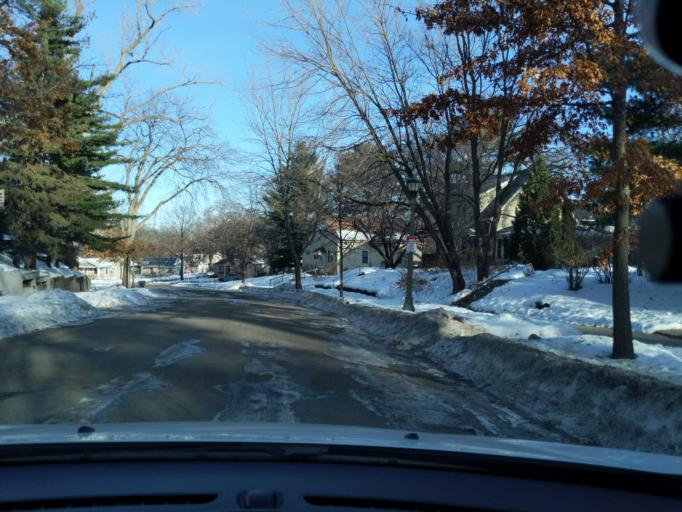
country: US
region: Minnesota
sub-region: Ramsey County
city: Lauderdale
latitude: 44.9825
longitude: -93.1987
